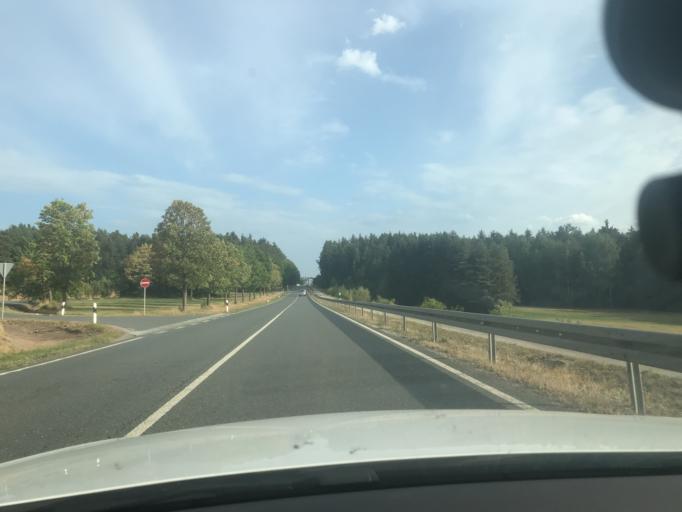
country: DE
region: Bavaria
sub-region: Upper Franconia
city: Emtmannsberg
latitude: 49.8998
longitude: 11.6096
